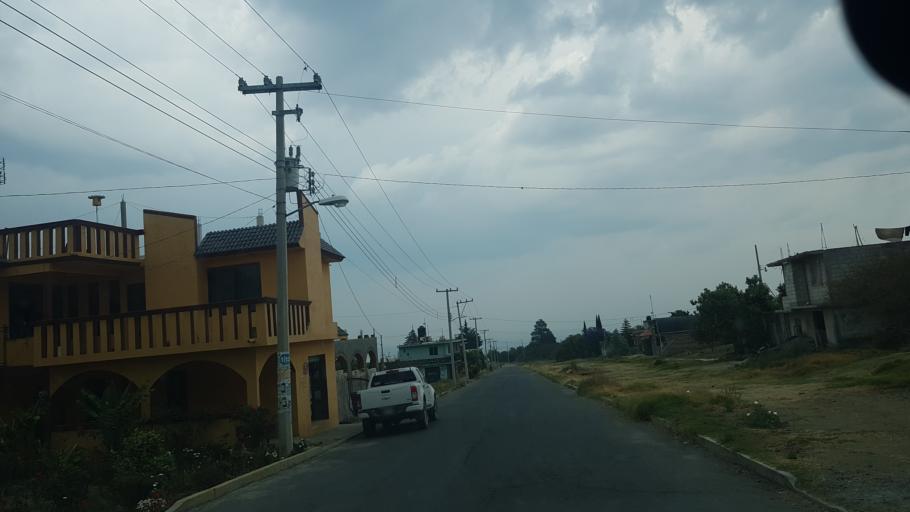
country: MX
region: Puebla
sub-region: Chiautzingo
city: San Nicolas Zecalacoayan
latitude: 19.1731
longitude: -98.4938
